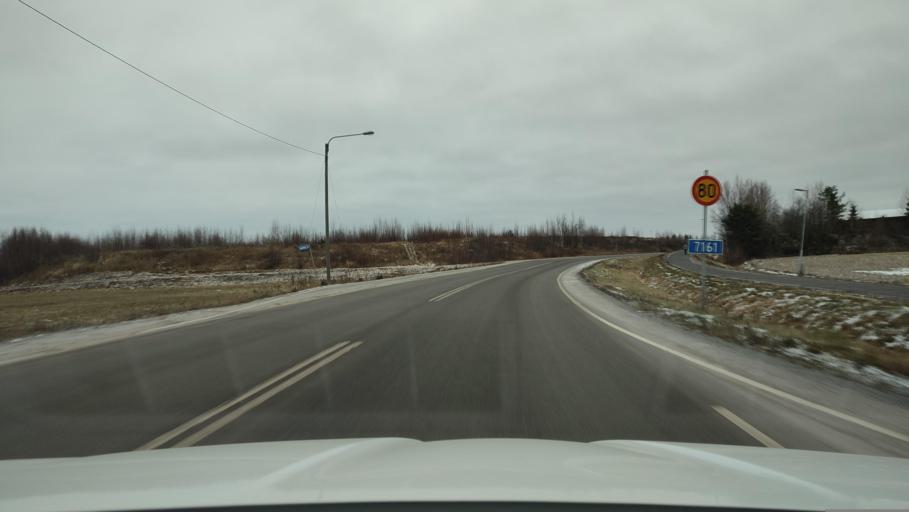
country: FI
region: Ostrobothnia
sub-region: Vaasa
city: Ristinummi
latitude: 63.0343
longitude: 21.7687
